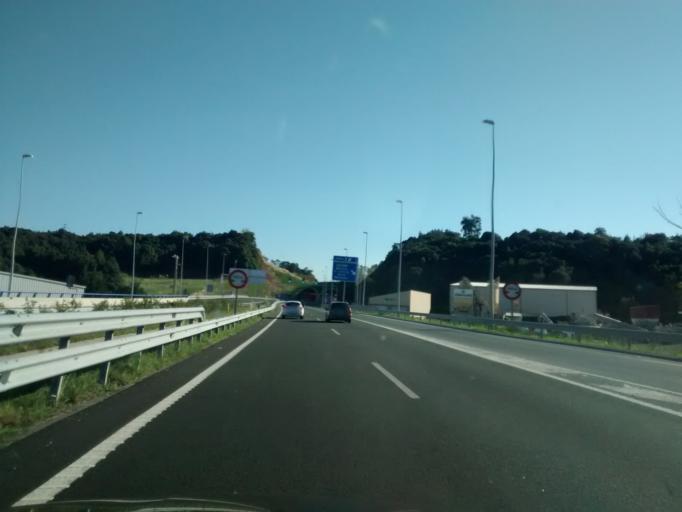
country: ES
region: Cantabria
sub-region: Provincia de Cantabria
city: Camargo
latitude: 43.4177
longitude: -3.8720
